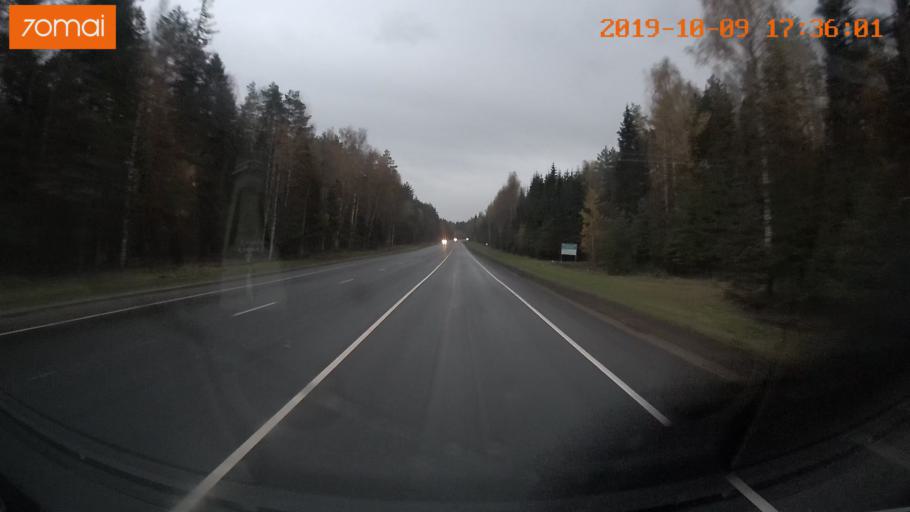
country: RU
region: Ivanovo
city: Bogorodskoye
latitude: 57.0847
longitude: 40.9985
